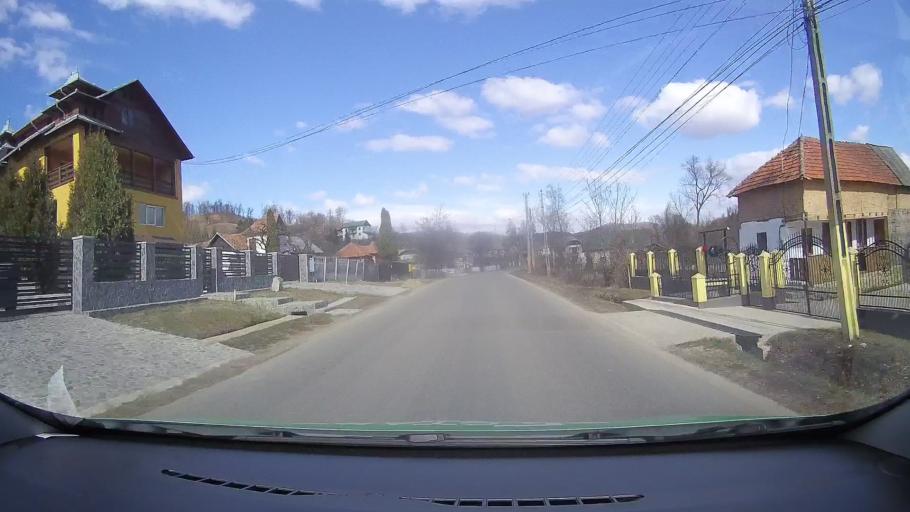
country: RO
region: Dambovita
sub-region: Comuna Vulcana Bai
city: Vulcana Bai
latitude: 45.0651
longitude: 25.3780
